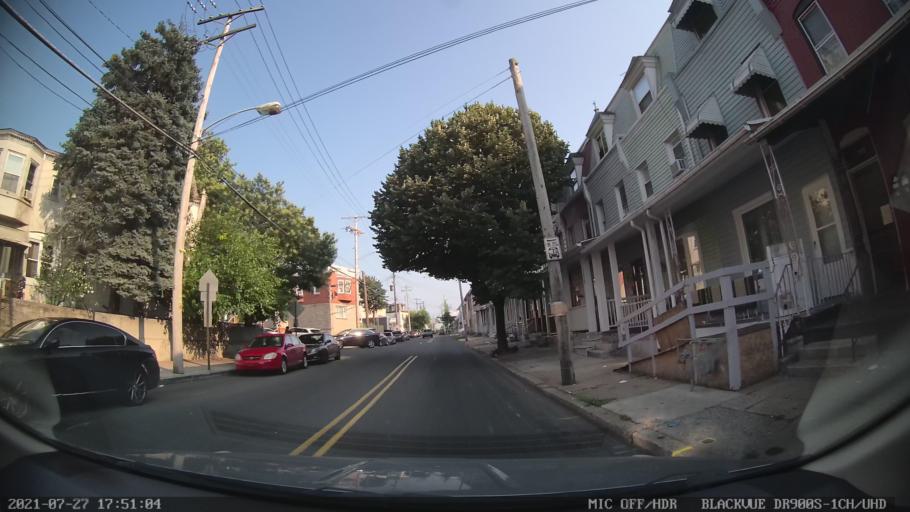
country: US
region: Pennsylvania
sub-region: Berks County
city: West Reading
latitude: 40.3479
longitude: -75.9417
